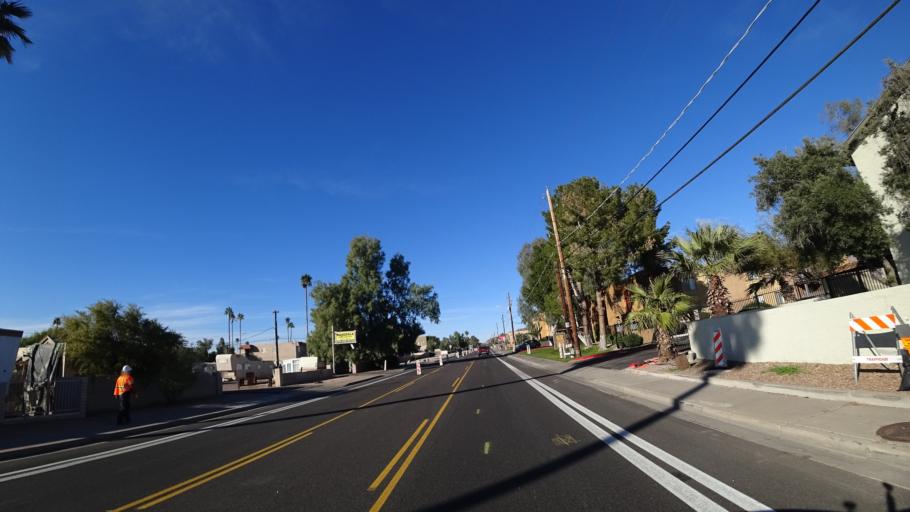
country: US
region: Arizona
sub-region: Maricopa County
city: Tempe Junction
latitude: 33.4594
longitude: -111.9784
